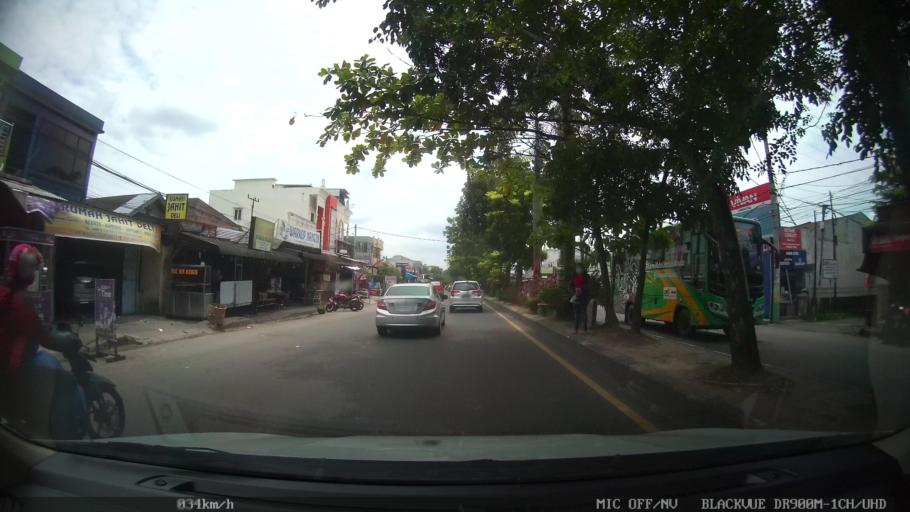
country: ID
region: North Sumatra
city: Deli Tua
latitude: 3.5321
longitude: 98.6443
